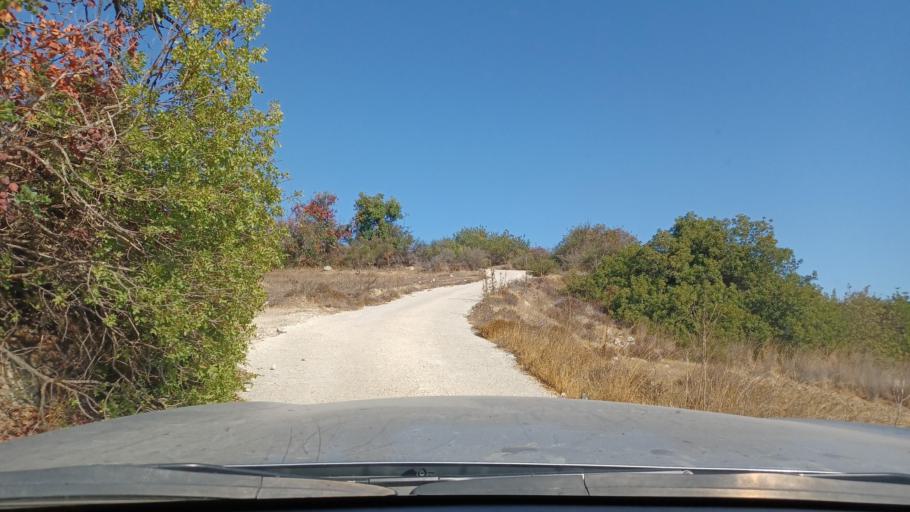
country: CY
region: Pafos
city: Polis
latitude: 35.0040
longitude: 32.4895
